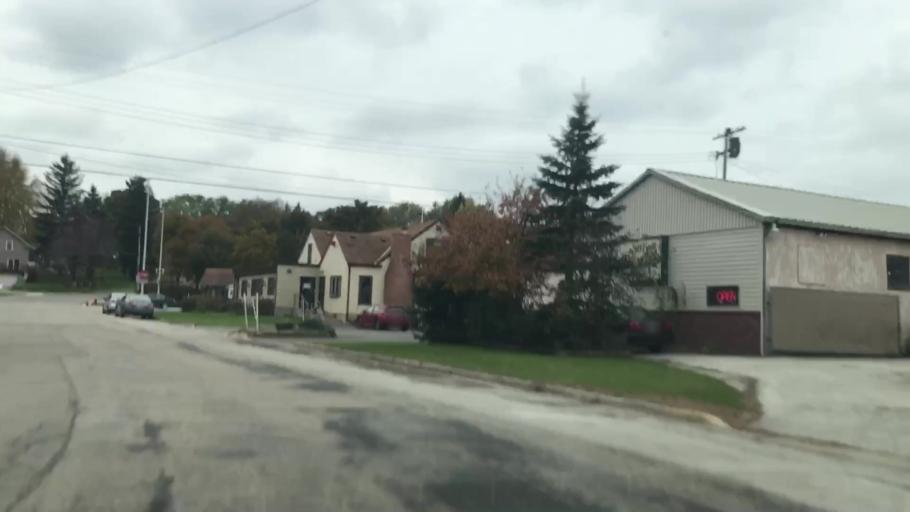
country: US
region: Wisconsin
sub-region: Waukesha County
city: Menomonee Falls
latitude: 43.1746
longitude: -88.1112
